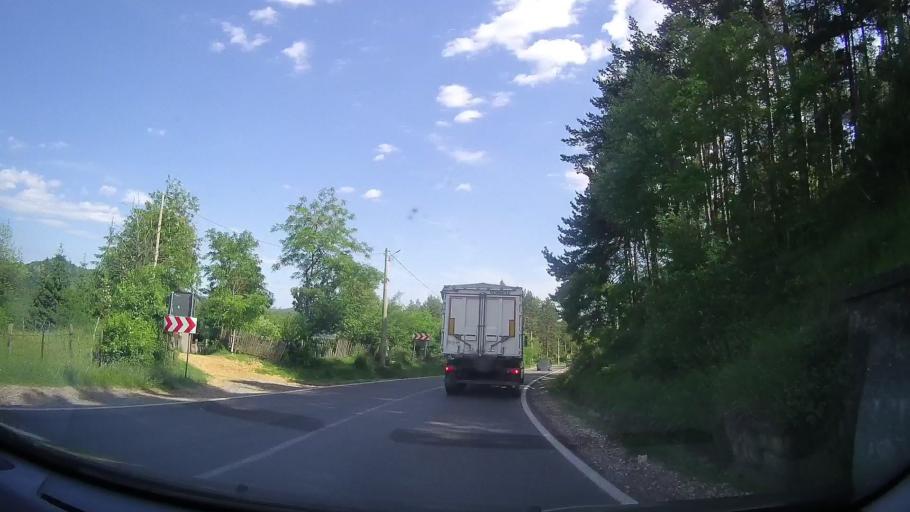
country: RO
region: Prahova
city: Maneciu
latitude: 45.3276
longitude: 25.9800
